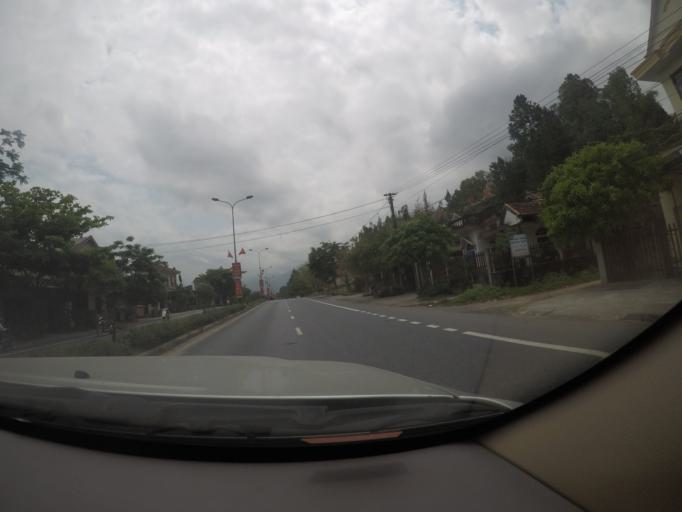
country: VN
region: Thua Thien-Hue
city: Phu Loc
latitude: 16.2793
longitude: 107.8612
